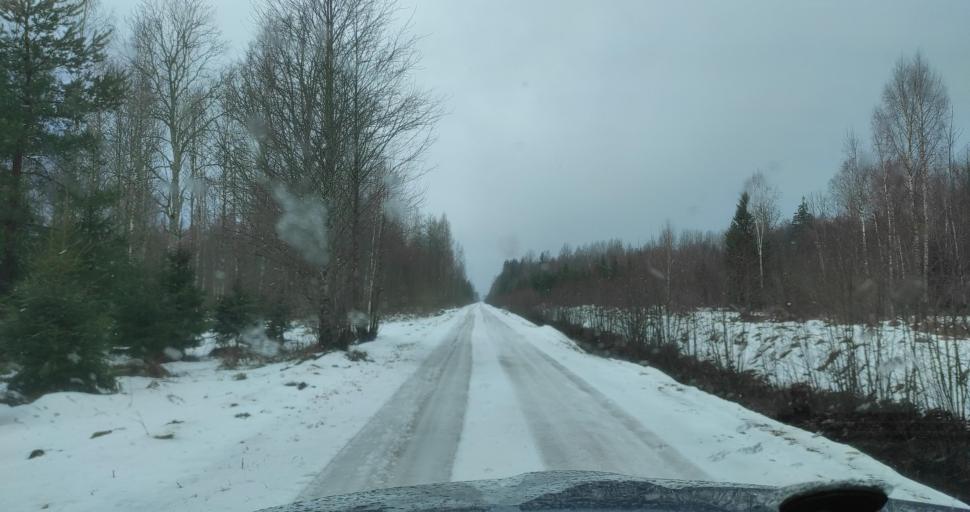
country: LV
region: Dundaga
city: Dundaga
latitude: 57.3884
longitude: 22.1376
